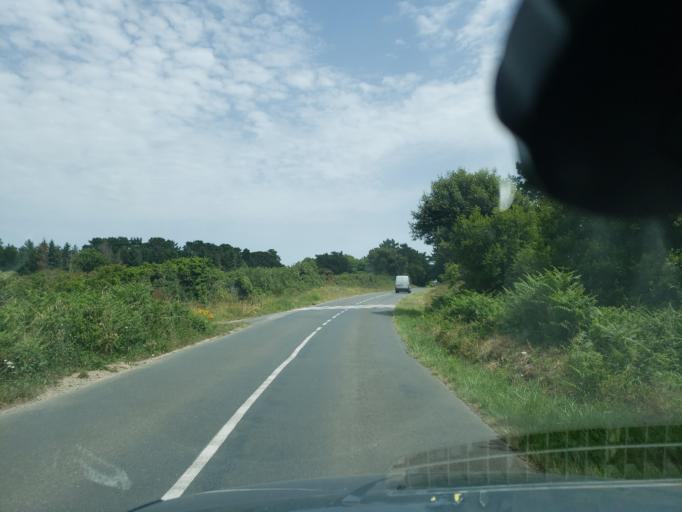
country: FR
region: Brittany
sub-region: Departement du Finistere
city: Treffiagat
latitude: 47.7993
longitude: -4.2436
